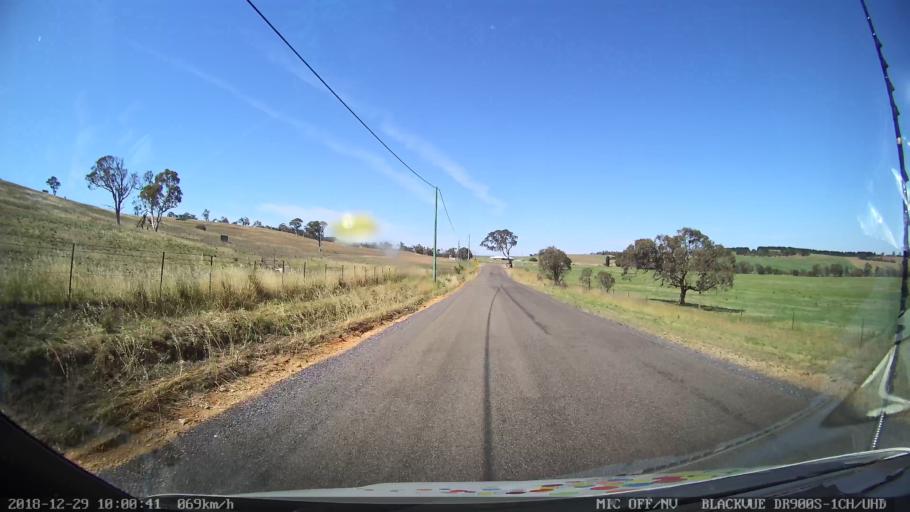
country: AU
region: New South Wales
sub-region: Goulburn Mulwaree
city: Goulburn
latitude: -34.7943
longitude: 149.4839
